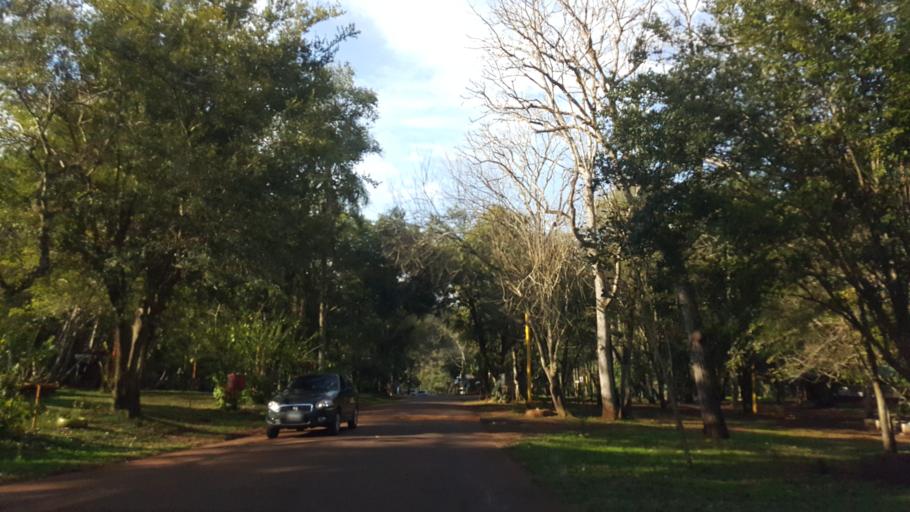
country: AR
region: Misiones
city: Puerto Leoni
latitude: -27.0006
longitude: -55.1802
